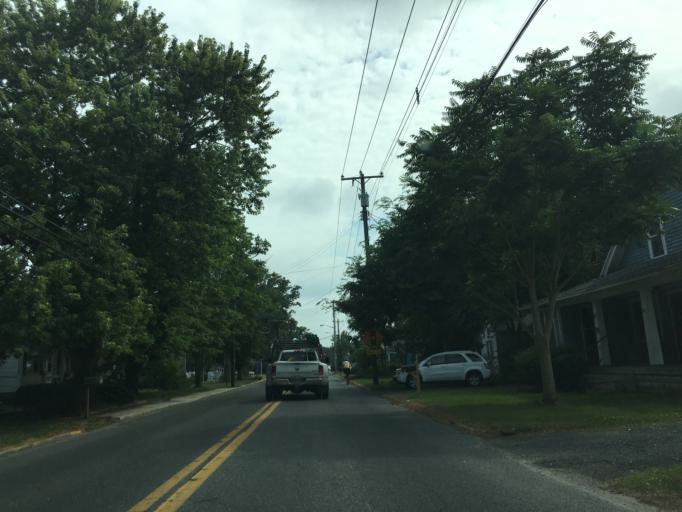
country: US
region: Delaware
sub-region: Sussex County
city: Ocean View
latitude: 38.5464
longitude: -75.0901
